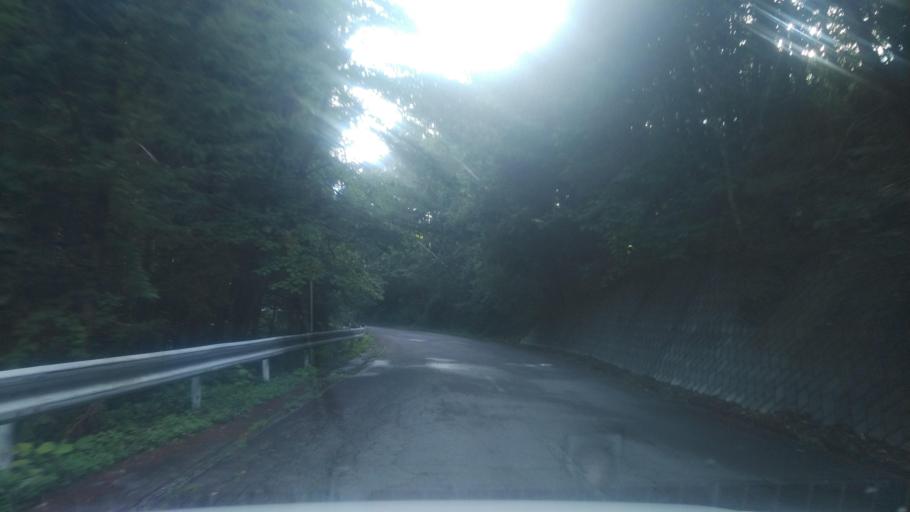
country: JP
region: Nagano
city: Ueda
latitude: 36.5100
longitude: 138.3750
